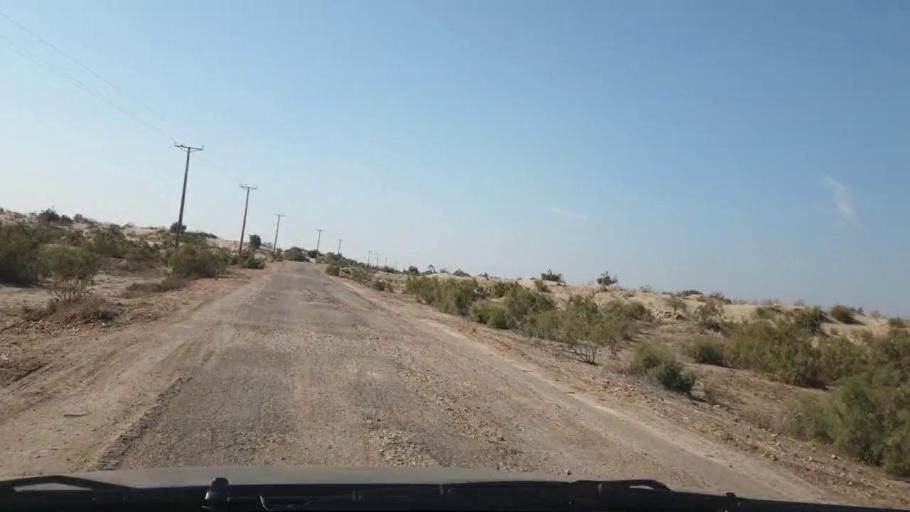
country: PK
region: Sindh
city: Khadro
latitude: 26.2681
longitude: 68.7976
